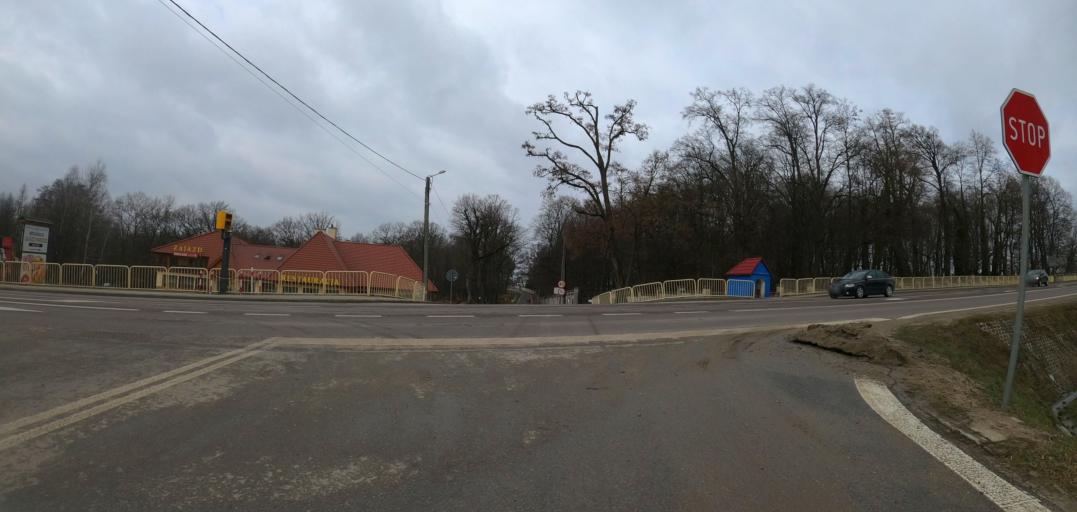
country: PL
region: Subcarpathian Voivodeship
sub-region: Powiat debicki
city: Pilzno
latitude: 49.9935
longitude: 21.3215
